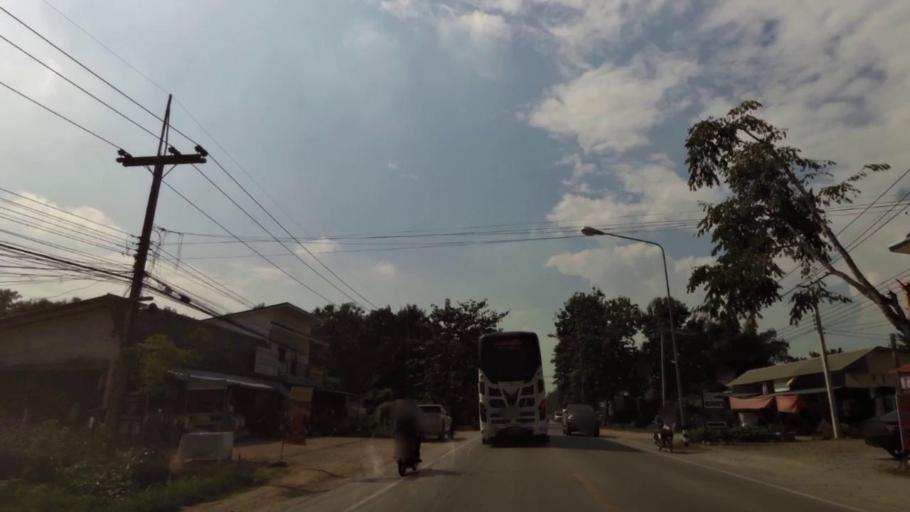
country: TH
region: Chiang Rai
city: Mae Lao
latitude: 19.8533
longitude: 99.7464
